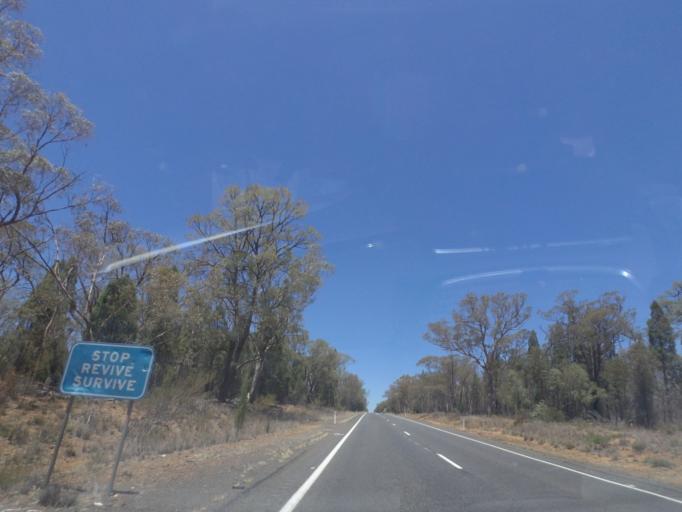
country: AU
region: New South Wales
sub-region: Warrumbungle Shire
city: Coonabarabran
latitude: -30.8512
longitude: 149.4581
